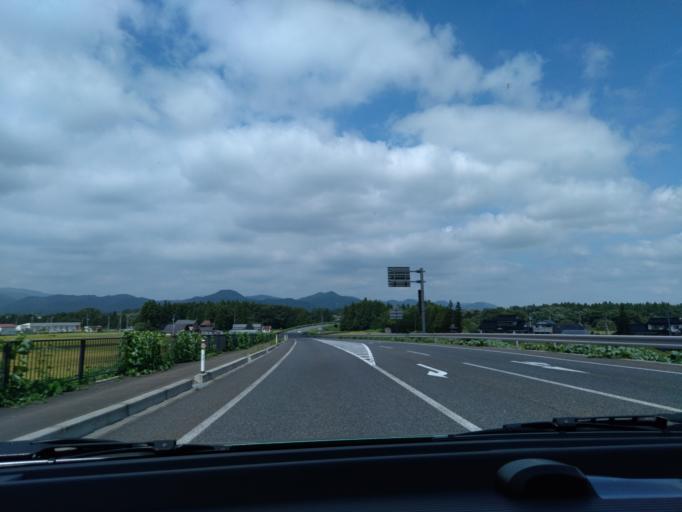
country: JP
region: Iwate
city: Hanamaki
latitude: 39.3741
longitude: 141.0570
